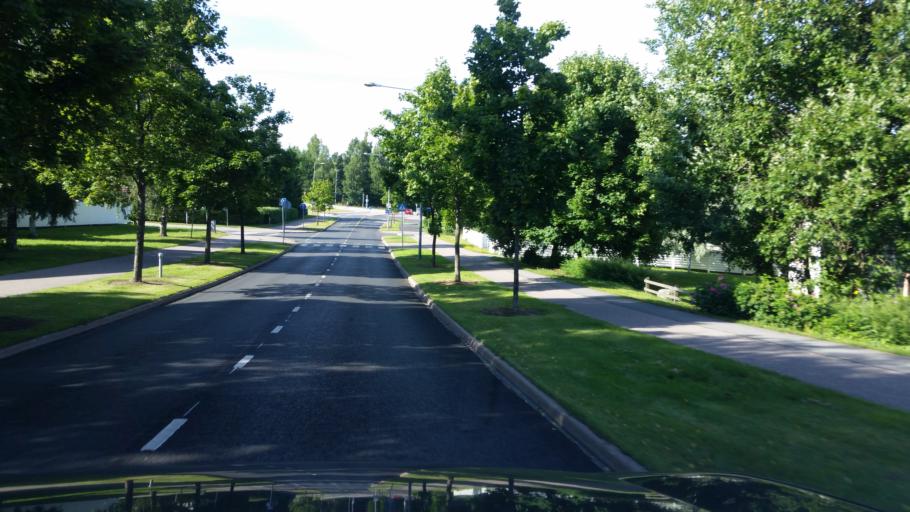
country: FI
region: Uusimaa
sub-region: Helsinki
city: Vantaa
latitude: 60.3212
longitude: 25.0133
